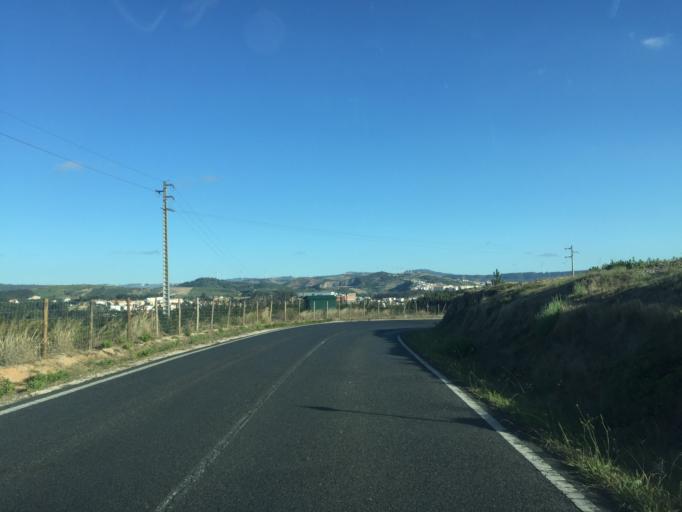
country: PT
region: Lisbon
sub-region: Torres Vedras
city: Torres Vedras
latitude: 39.1156
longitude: -9.2615
